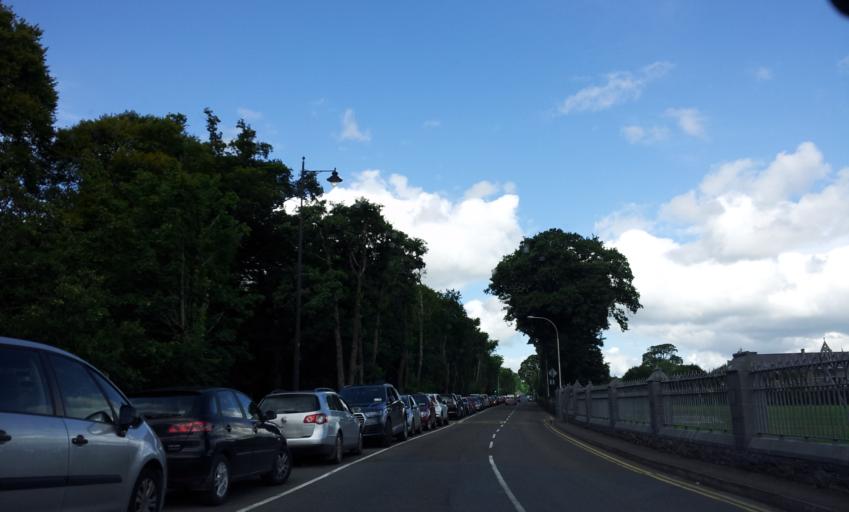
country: IE
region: Munster
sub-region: Ciarrai
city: Cill Airne
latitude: 52.0593
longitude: -9.5192
